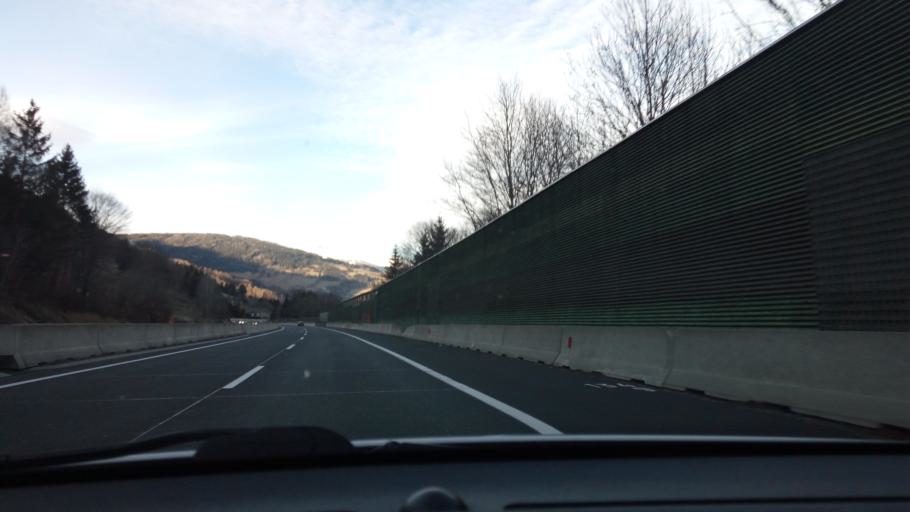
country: AT
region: Carinthia
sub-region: Politischer Bezirk Spittal an der Drau
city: Trebesing
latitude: 46.8657
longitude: 13.5051
